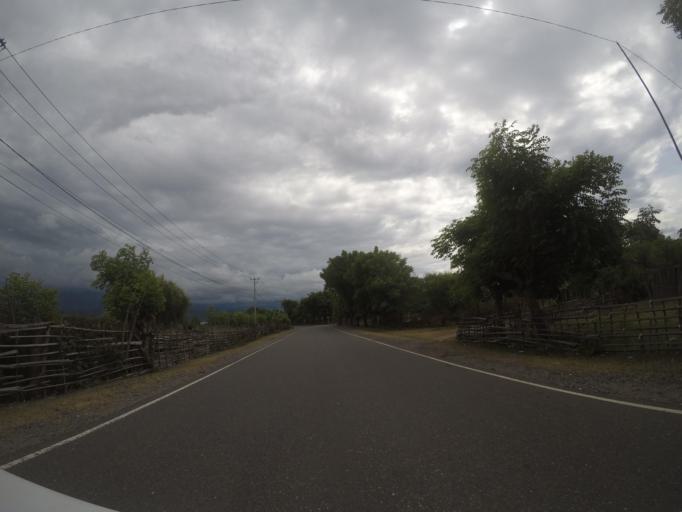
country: TL
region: Liquica
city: Maubara
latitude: -8.7574
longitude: 125.1006
